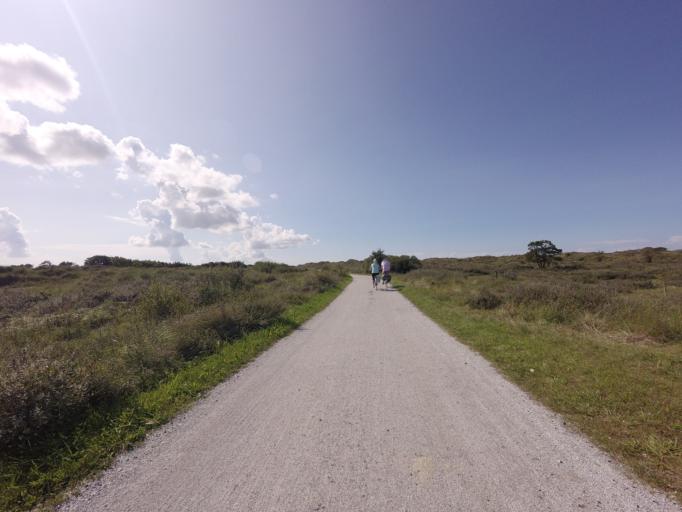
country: NL
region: Friesland
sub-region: Gemeente Terschelling
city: West-Terschelling
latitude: 53.4095
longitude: 5.3992
